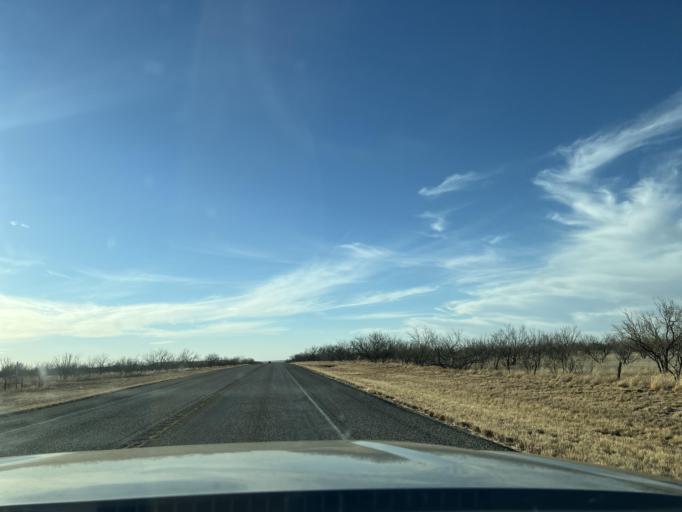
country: US
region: Texas
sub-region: Borden County
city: Gail
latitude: 32.7683
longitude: -101.3113
